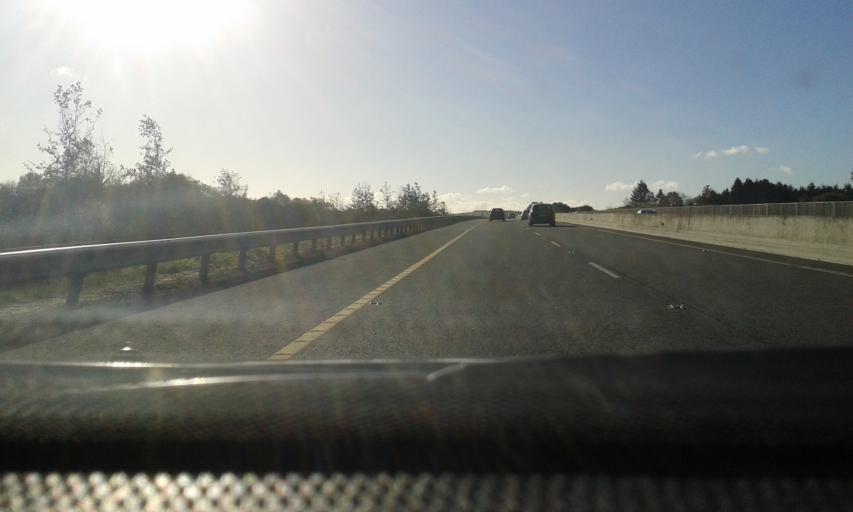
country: IE
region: Leinster
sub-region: Laois
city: Mountrath
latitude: 52.9571
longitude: -7.4418
